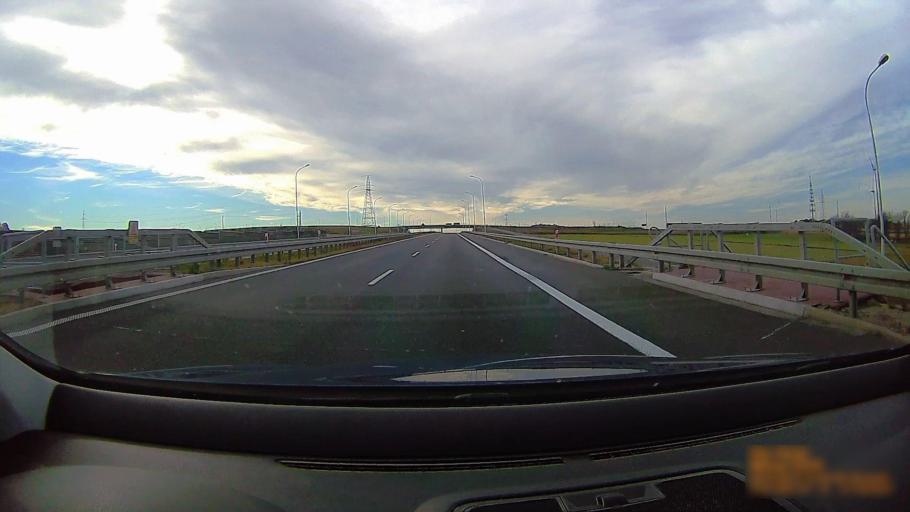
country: PL
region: Greater Poland Voivodeship
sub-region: Powiat ostrowski
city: Przygodzice
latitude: 51.6336
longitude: 17.8712
